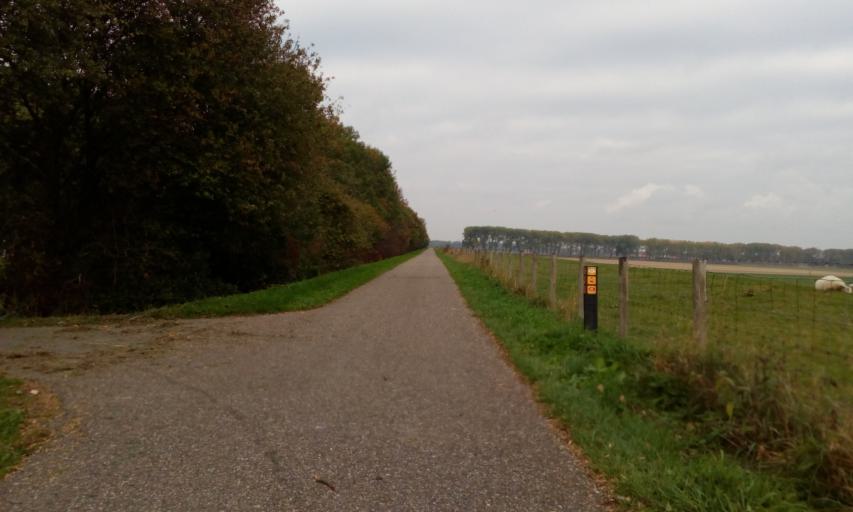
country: NL
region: South Holland
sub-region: Gemeente Binnenmaas
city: Heinenoord
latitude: 51.8381
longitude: 4.4584
